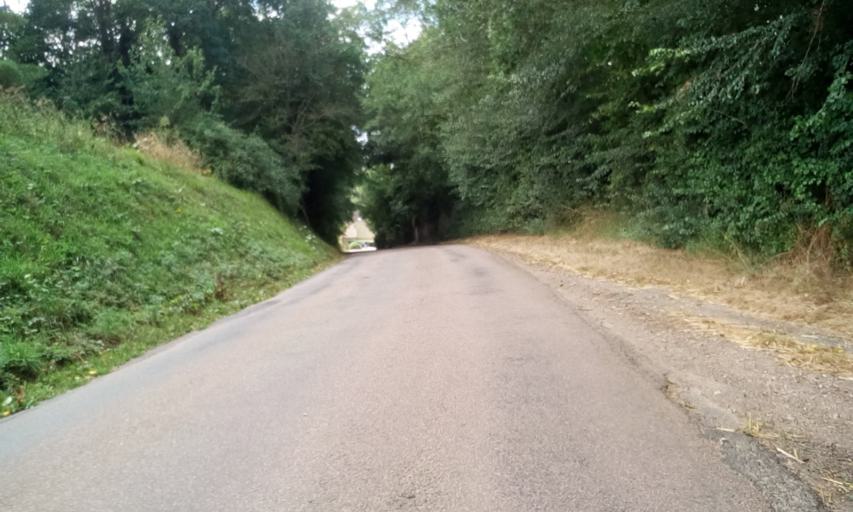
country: FR
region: Lower Normandy
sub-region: Departement du Calvados
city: Thaon
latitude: 49.2933
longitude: -0.4856
